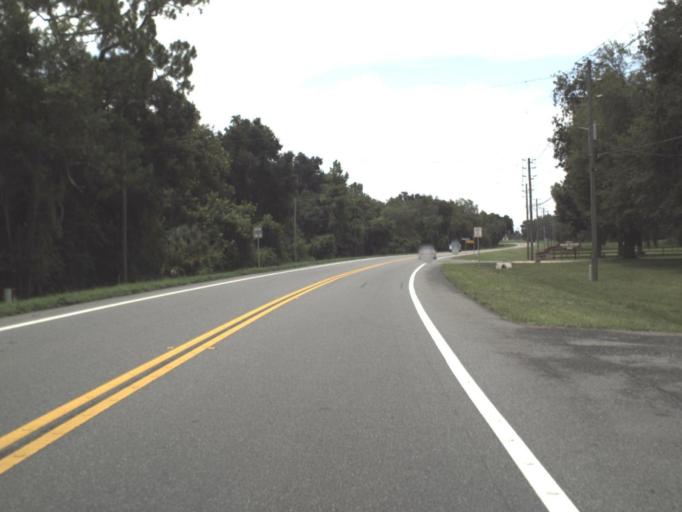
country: US
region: Florida
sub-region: Pasco County
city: Lacoochee
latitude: 28.4850
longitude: -82.1967
